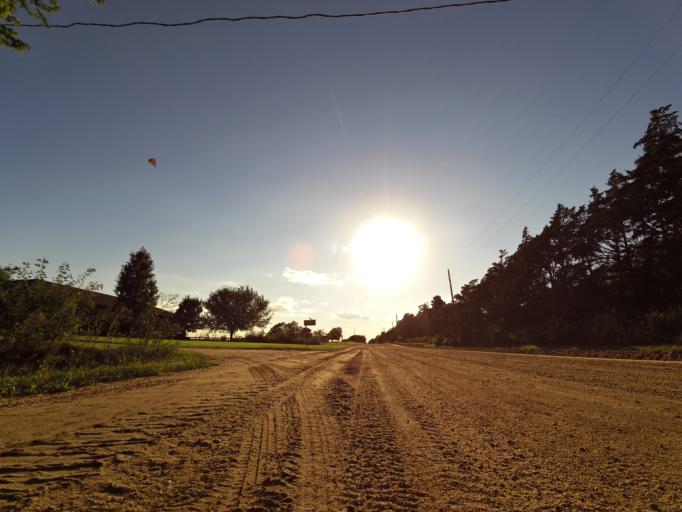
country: US
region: Kansas
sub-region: Reno County
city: South Hutchinson
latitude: 37.9992
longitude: -98.0423
